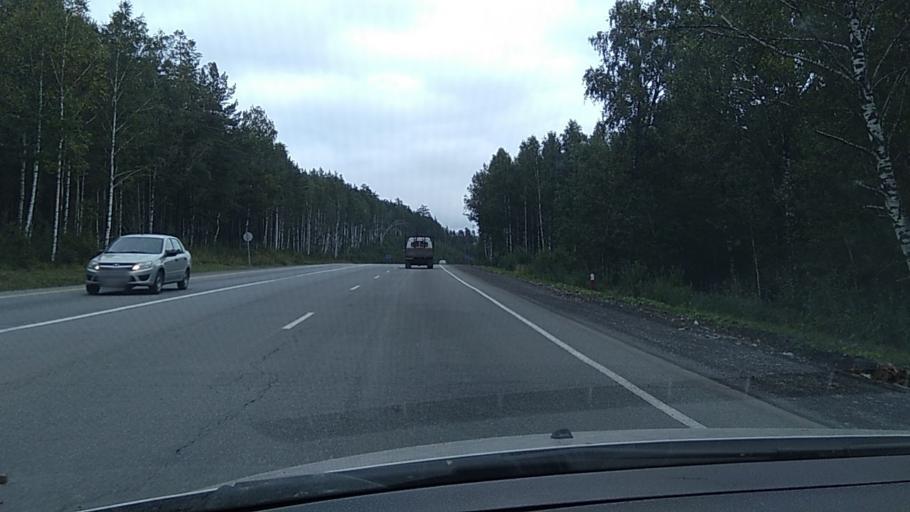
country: RU
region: Chelyabinsk
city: Zlatoust
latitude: 55.0544
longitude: 59.7113
